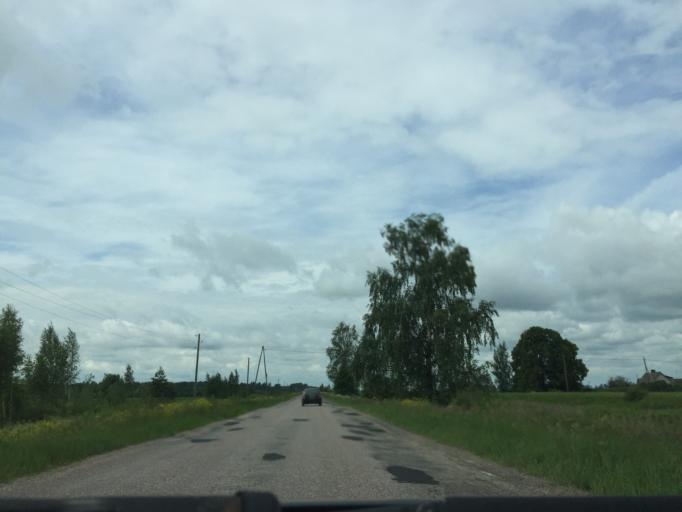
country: LV
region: Jelgava
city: Jelgava
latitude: 56.6634
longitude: 23.5614
